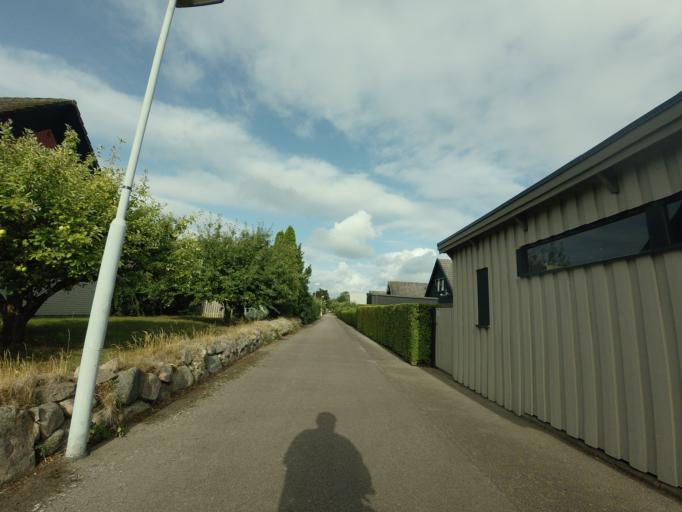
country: SE
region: Skane
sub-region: Hoganas Kommun
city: Hoganas
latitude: 56.1593
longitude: 12.5773
